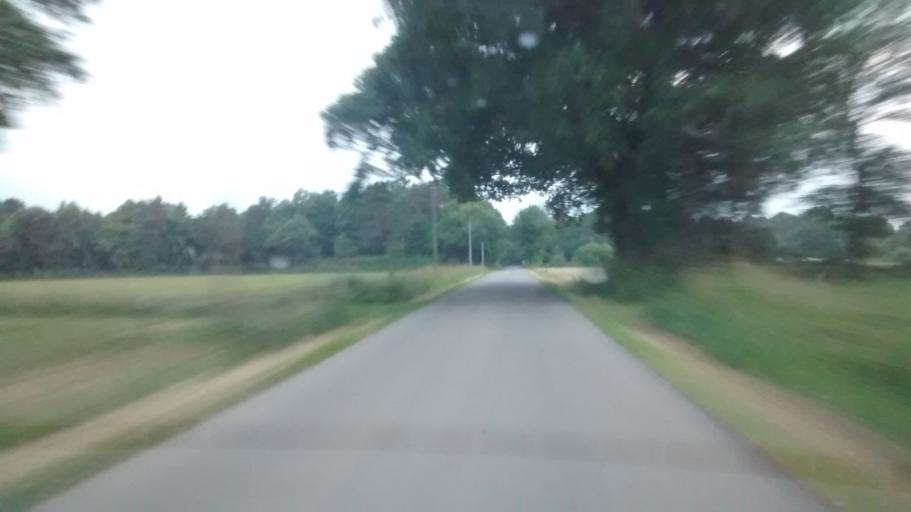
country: FR
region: Brittany
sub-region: Departement du Morbihan
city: Molac
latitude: 47.7269
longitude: -2.3977
